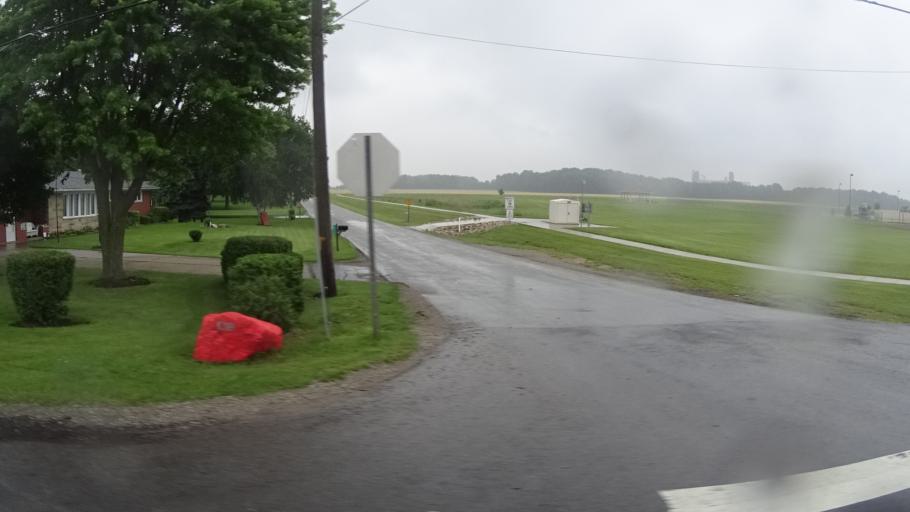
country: US
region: Ohio
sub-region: Huron County
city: Bellevue
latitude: 41.2952
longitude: -82.8335
